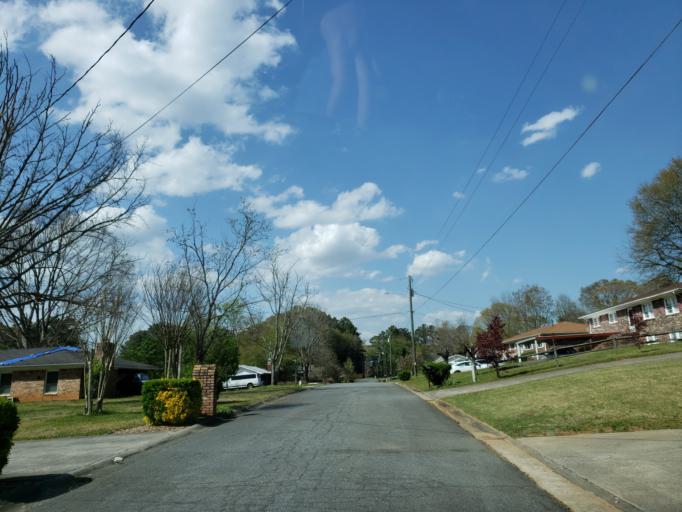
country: US
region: Georgia
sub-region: Cobb County
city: Kennesaw
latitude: 34.0298
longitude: -84.5470
